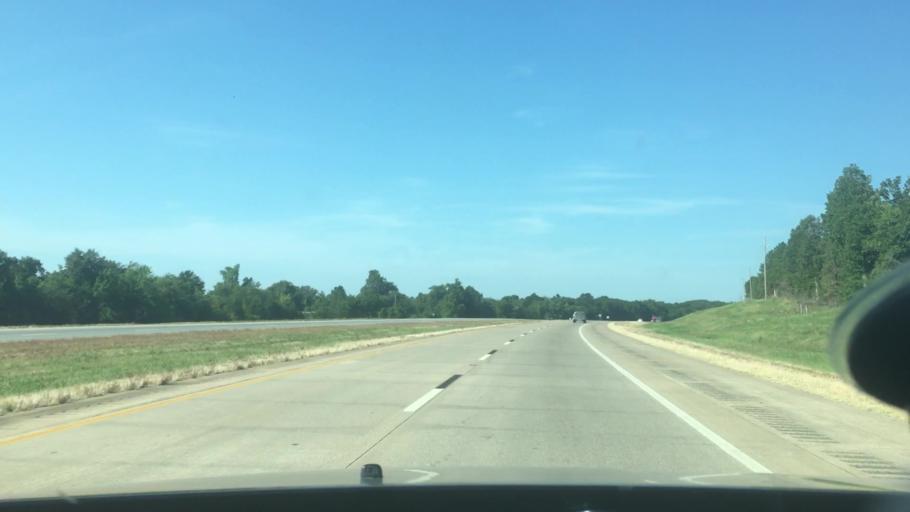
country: US
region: Oklahoma
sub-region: Atoka County
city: Atoka
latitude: 34.3067
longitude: -96.1778
